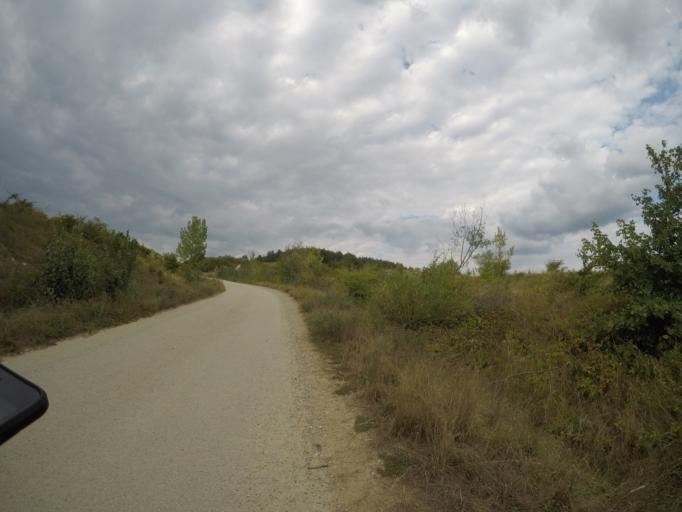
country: SK
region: Trenciansky
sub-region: Okres Trencin
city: Trencin
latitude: 48.9094
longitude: 17.9994
